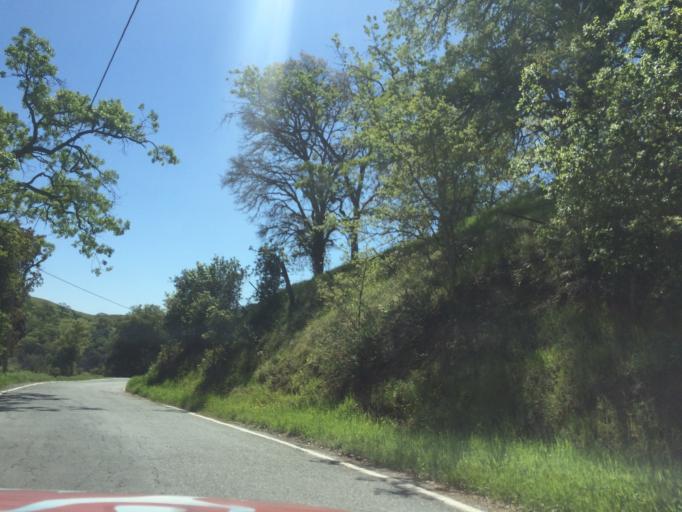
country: US
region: California
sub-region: Santa Clara County
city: Morgan Hill
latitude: 37.1755
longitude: -121.5691
